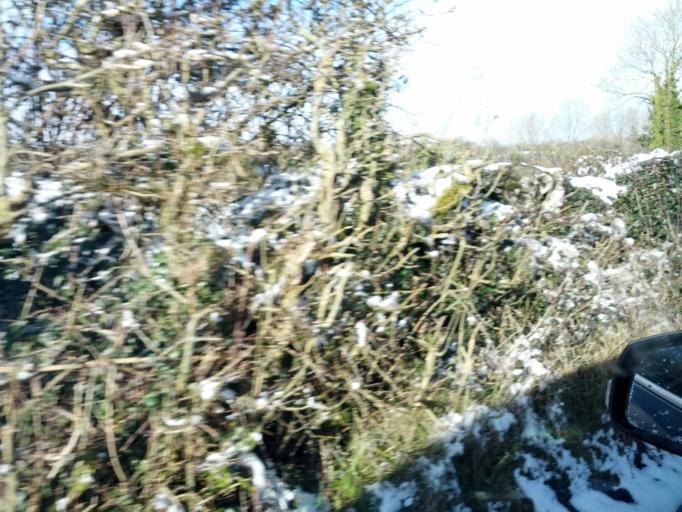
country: IE
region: Connaught
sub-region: County Galway
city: Athenry
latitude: 53.2076
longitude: -8.8116
